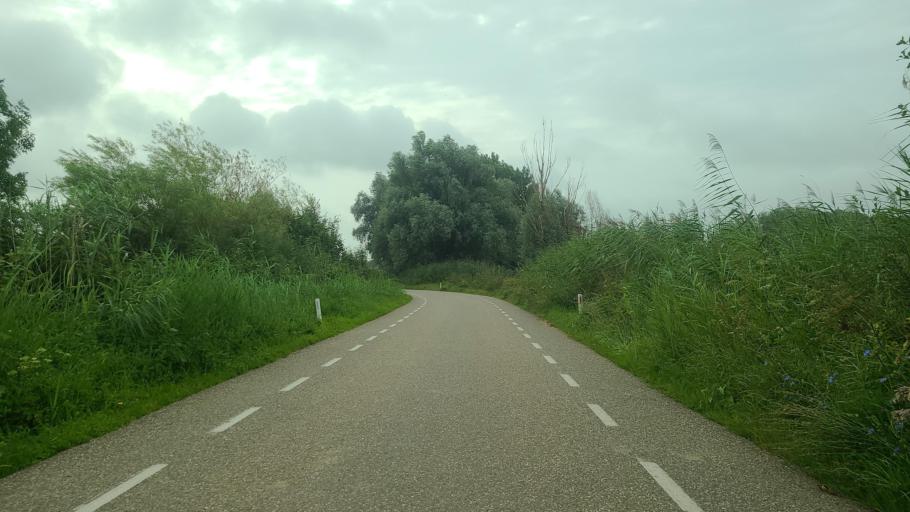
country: NL
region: Gelderland
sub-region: Gemeente Groesbeek
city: Berg en Dal
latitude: 51.8418
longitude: 5.9770
